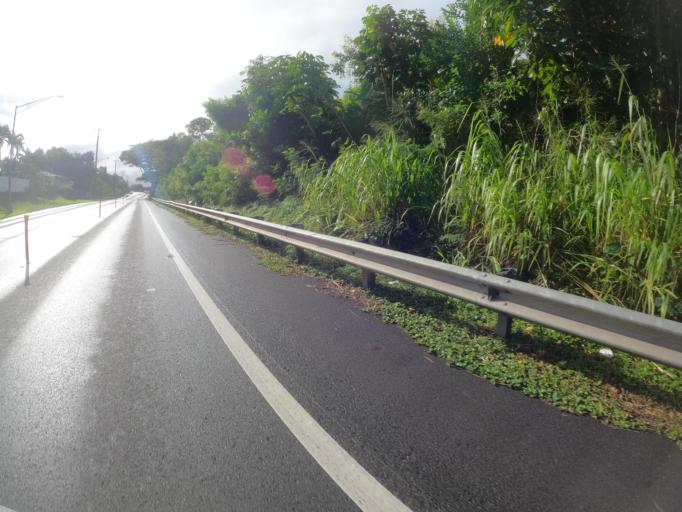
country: US
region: Hawaii
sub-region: Honolulu County
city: He'eia
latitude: 21.4200
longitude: -157.8155
